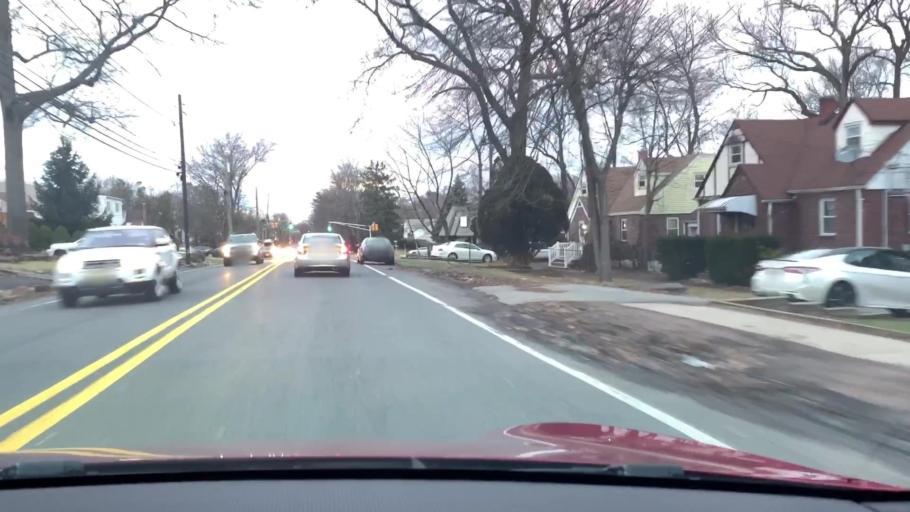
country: US
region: New Jersey
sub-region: Bergen County
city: Demarest
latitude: 40.9464
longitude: -73.9763
